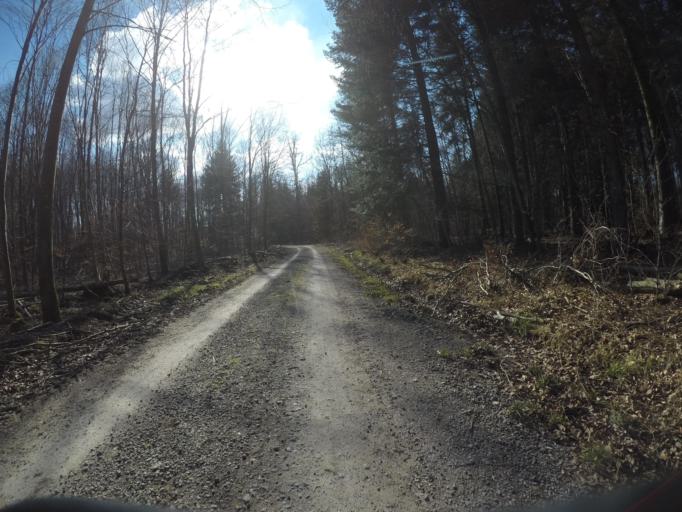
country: DE
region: Baden-Wuerttemberg
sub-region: Tuebingen Region
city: Dusslingen
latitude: 48.4597
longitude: 9.0199
